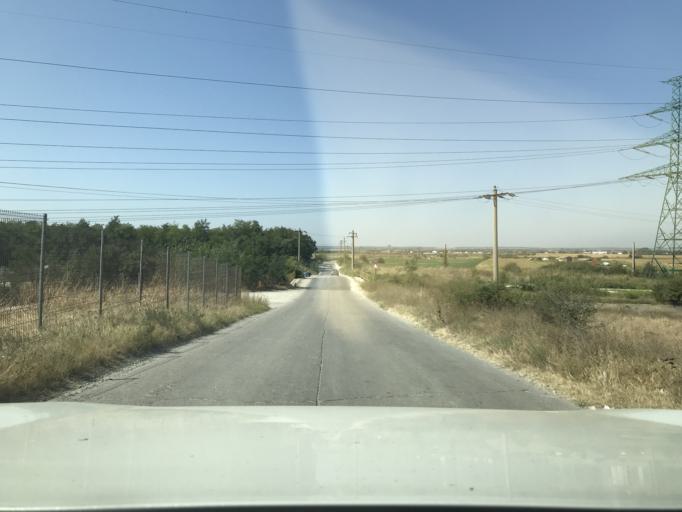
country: RO
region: Olt
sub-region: Comuna Slatioara
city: Slatioara
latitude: 44.3933
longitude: 24.3443
